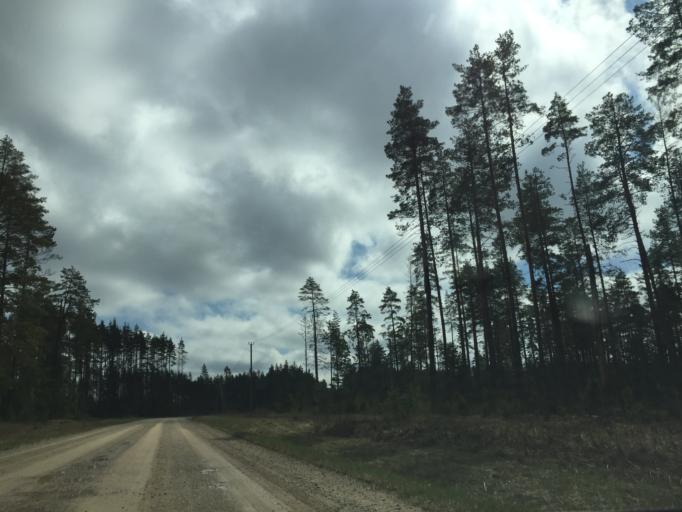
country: EE
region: Valgamaa
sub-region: Valga linn
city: Valga
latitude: 57.6505
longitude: 26.2191
